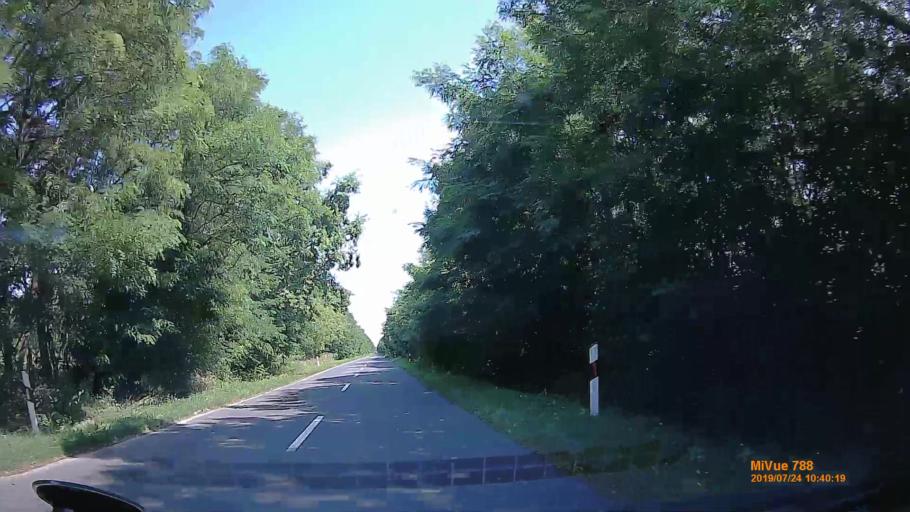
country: HU
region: Szabolcs-Szatmar-Bereg
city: Tarpa
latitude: 48.1736
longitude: 22.5448
